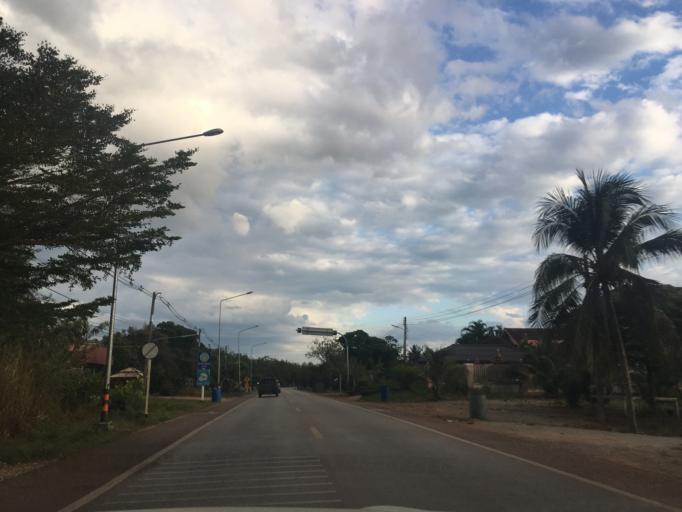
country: TH
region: Rayong
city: Klaeng
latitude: 12.7464
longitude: 101.7336
